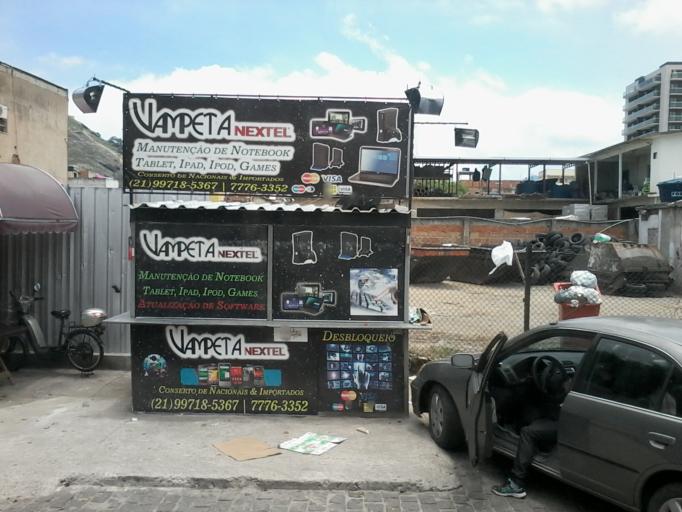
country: BR
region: Rio de Janeiro
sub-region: Nilopolis
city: Nilopolis
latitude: -23.0246
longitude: -43.4817
